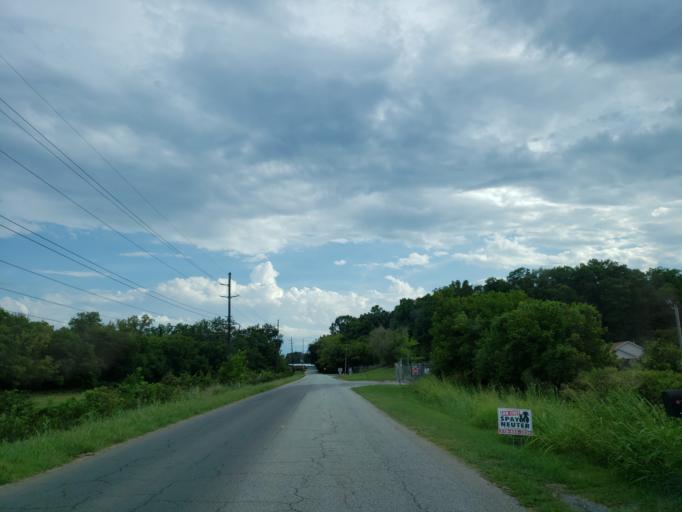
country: US
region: Georgia
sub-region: Bartow County
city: Cartersville
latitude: 34.1523
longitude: -84.8295
